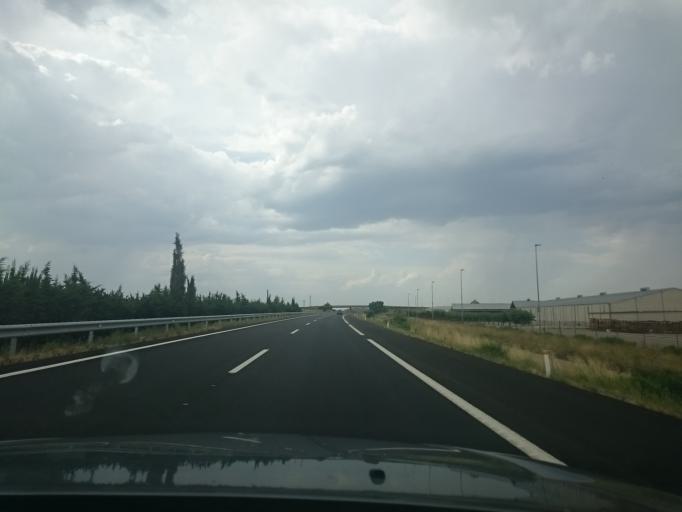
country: ES
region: La Rioja
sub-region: Provincia de La Rioja
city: Aldeanueva de Ebro
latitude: 42.2219
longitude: -1.8952
